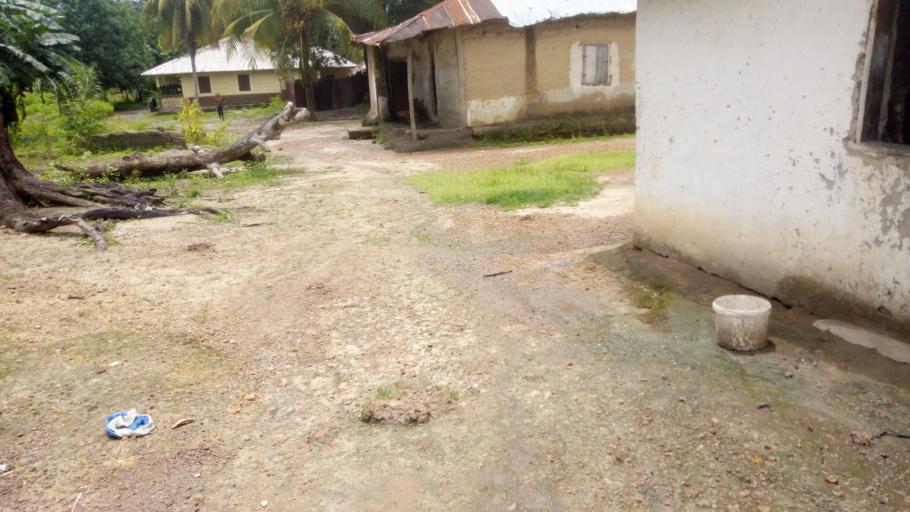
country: SL
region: Northern Province
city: Magburaka
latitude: 8.7158
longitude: -11.9531
